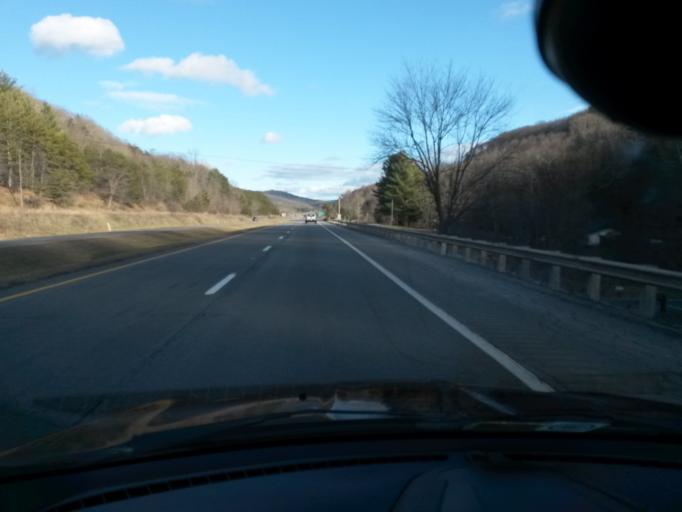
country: US
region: West Virginia
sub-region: Mercer County
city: Athens
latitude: 37.3421
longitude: -80.9954
